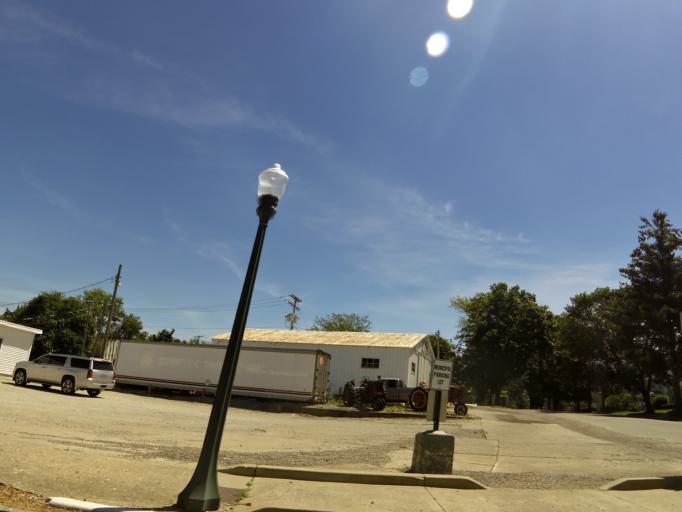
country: US
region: Illinois
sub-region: Vermilion County
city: Rossville
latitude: 40.3780
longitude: -87.6683
